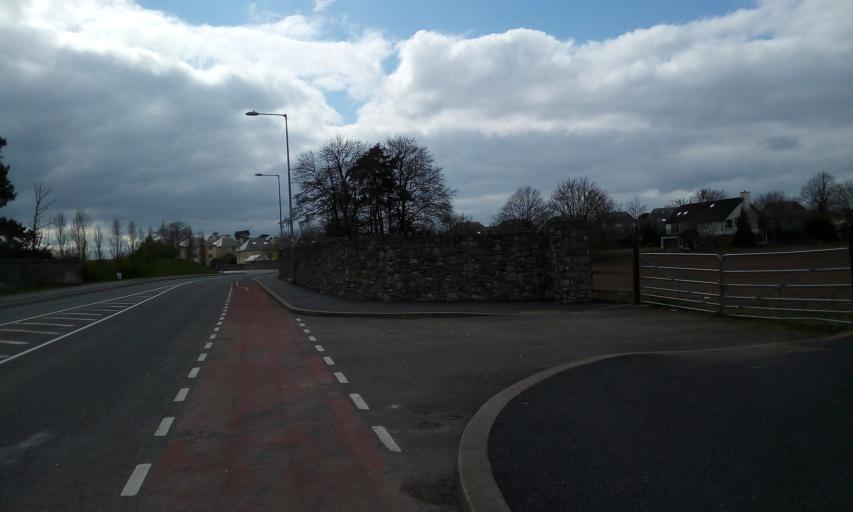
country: IE
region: Leinster
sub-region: Kilkenny
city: Kilkenny
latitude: 52.6419
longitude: -7.2552
